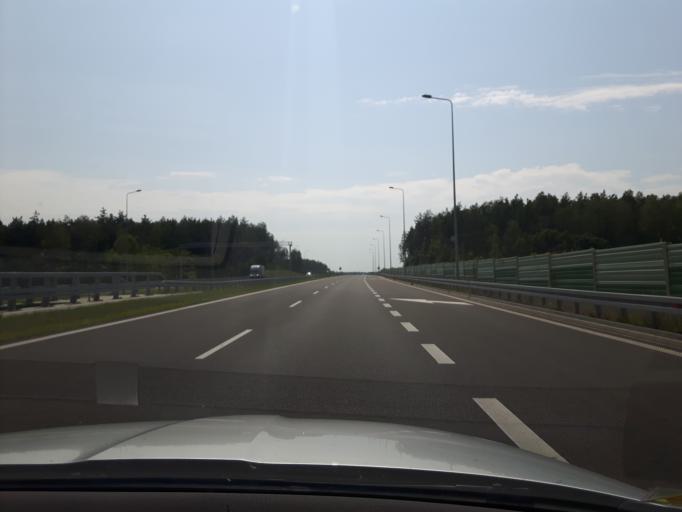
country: PL
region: Warmian-Masurian Voivodeship
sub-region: Powiat nidzicki
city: Nidzica
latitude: 53.2741
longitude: 20.4354
